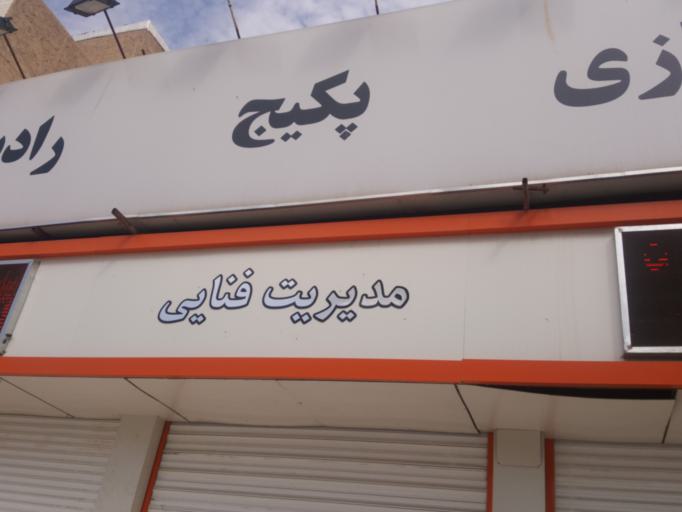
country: IR
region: Fars
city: Marvdasht
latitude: 29.8810
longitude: 52.8090
